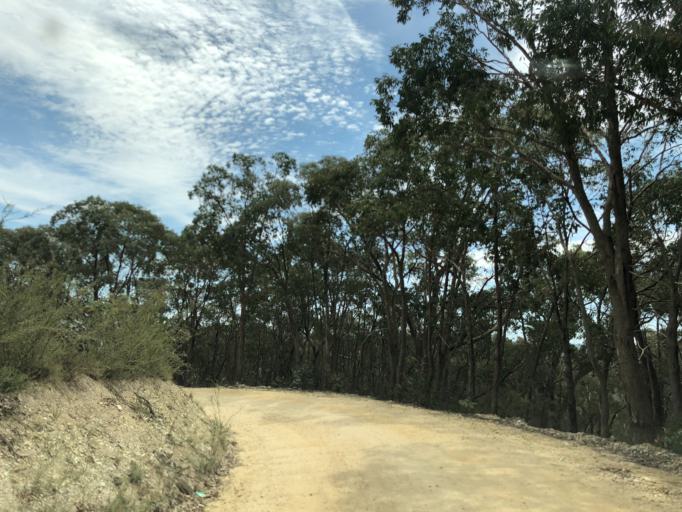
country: AU
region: Victoria
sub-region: Moorabool
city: Bacchus Marsh
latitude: -37.4932
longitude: 144.3723
